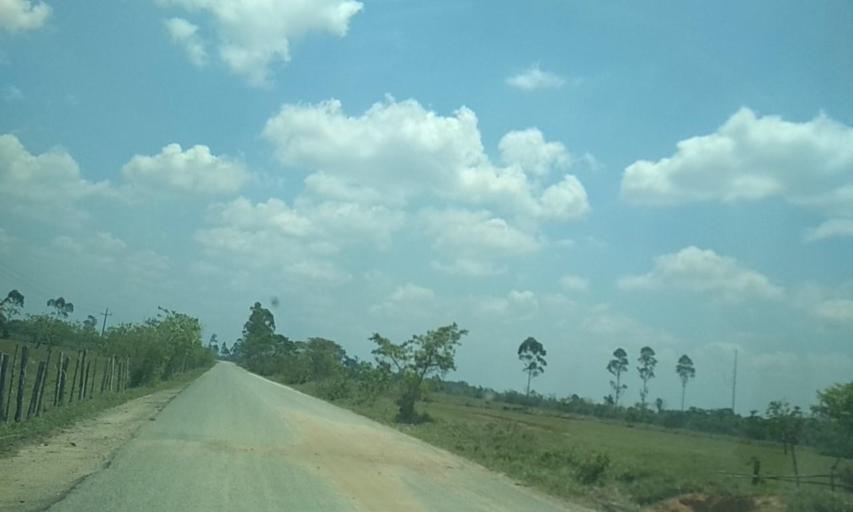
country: MX
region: Tabasco
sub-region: Huimanguillo
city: Francisco Rueda
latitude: 17.8115
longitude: -93.8689
